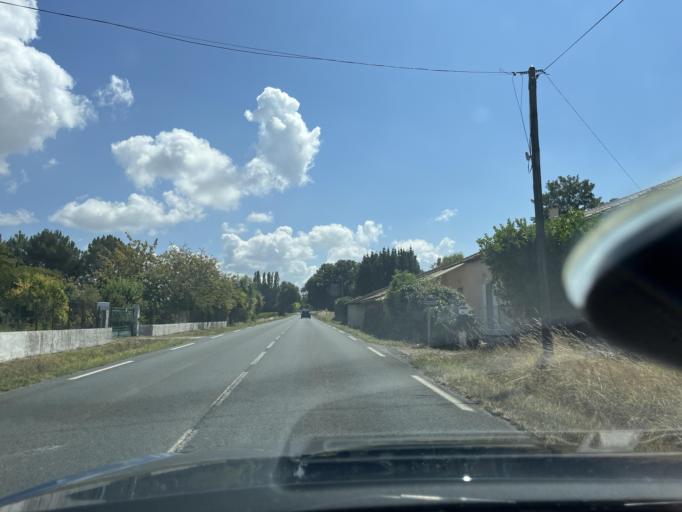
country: FR
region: Aquitaine
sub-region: Departement de la Gironde
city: Cantenac
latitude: 45.0718
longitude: -0.6278
